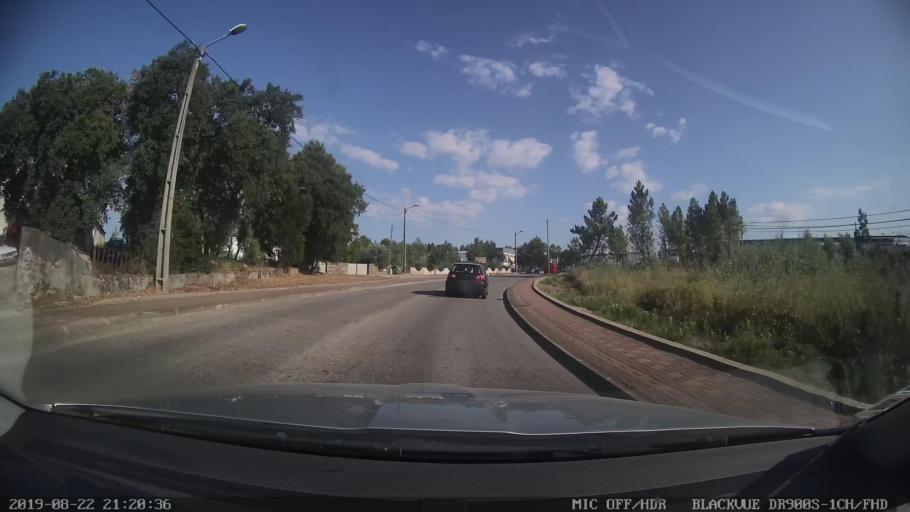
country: PT
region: Castelo Branco
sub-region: Serta
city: Serta
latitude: 39.8136
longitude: -8.1089
